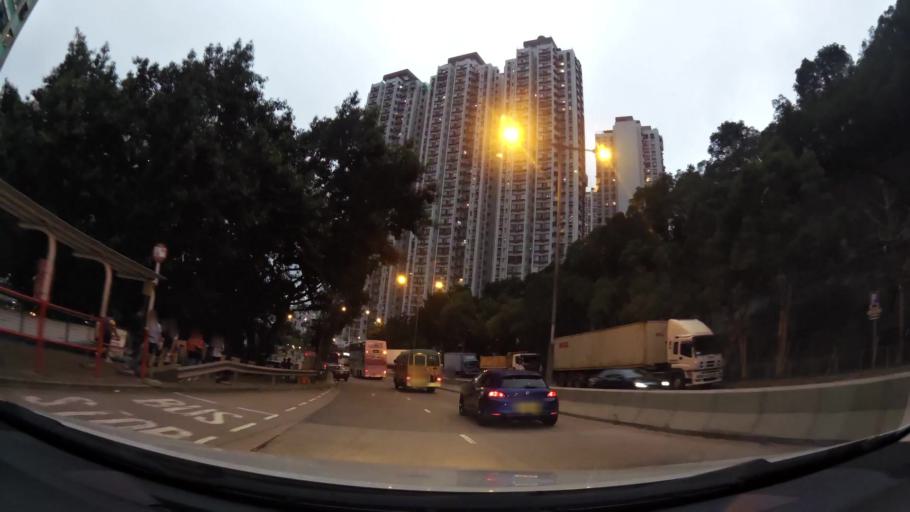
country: HK
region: Tsuen Wan
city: Tsuen Wan
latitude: 22.3456
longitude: 114.1078
